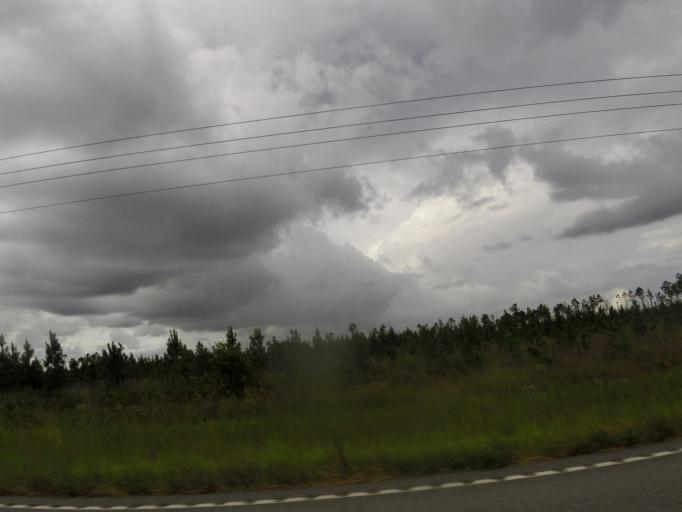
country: US
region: Florida
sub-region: Baker County
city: Macclenny
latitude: 30.5173
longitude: -82.1078
